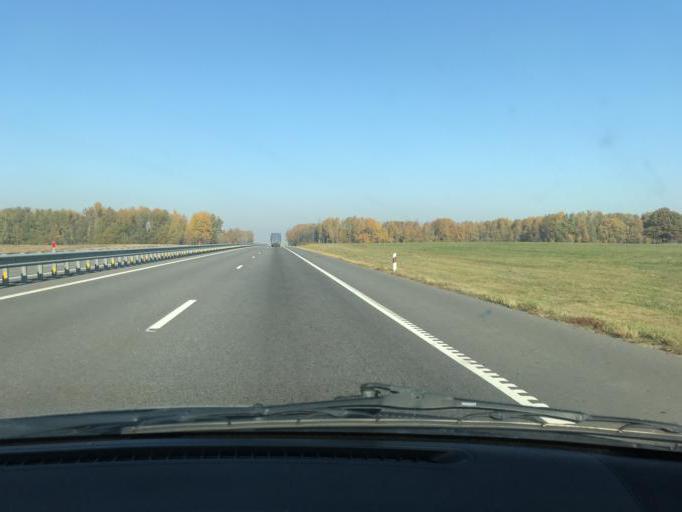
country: BY
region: Minsk
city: Slutsk
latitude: 53.1943
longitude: 27.5512
